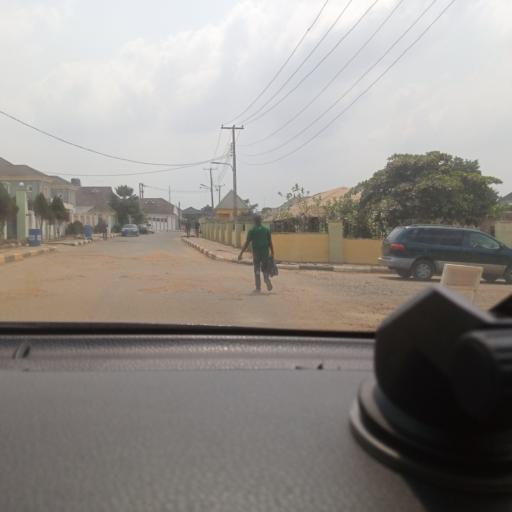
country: NG
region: Oyo
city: Ibadan
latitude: 7.4298
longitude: 3.9061
